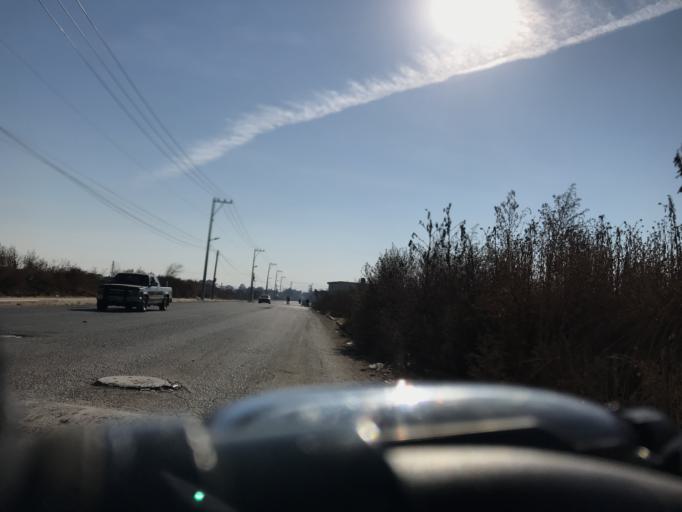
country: MX
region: Mexico
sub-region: Tonanitla
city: Colonia la Asuncion
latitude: 19.6909
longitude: -99.0596
